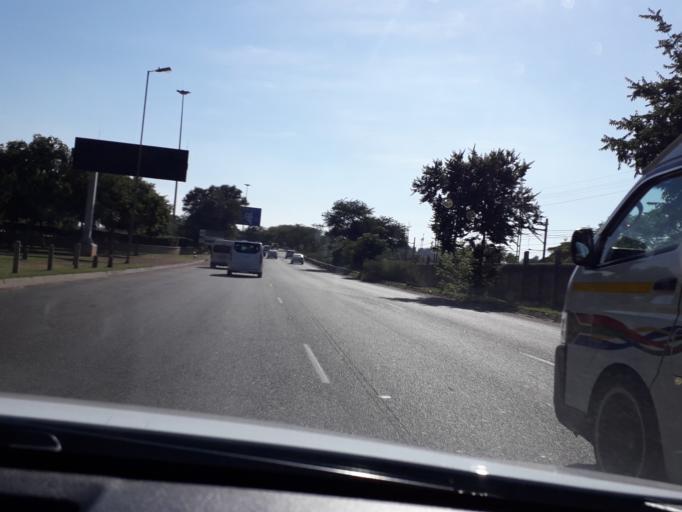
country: ZA
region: Gauteng
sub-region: City of Tshwane Metropolitan Municipality
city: Pretoria
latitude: -25.7445
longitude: 28.2463
